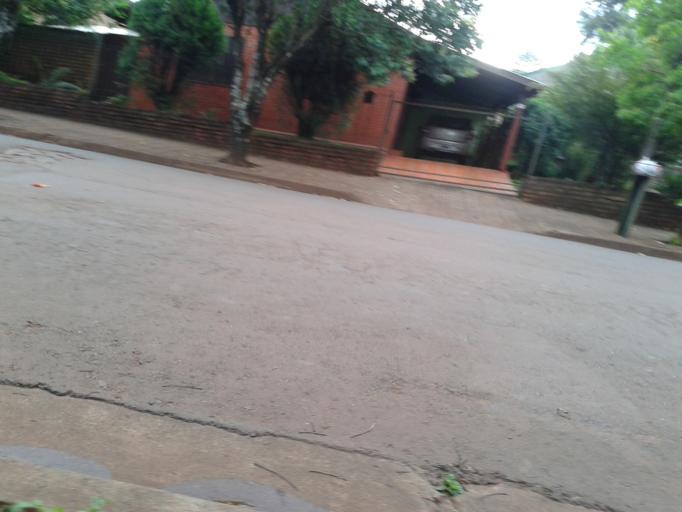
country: AR
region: Misiones
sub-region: Departamento de Obera
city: Obera
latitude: -27.4834
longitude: -55.1118
